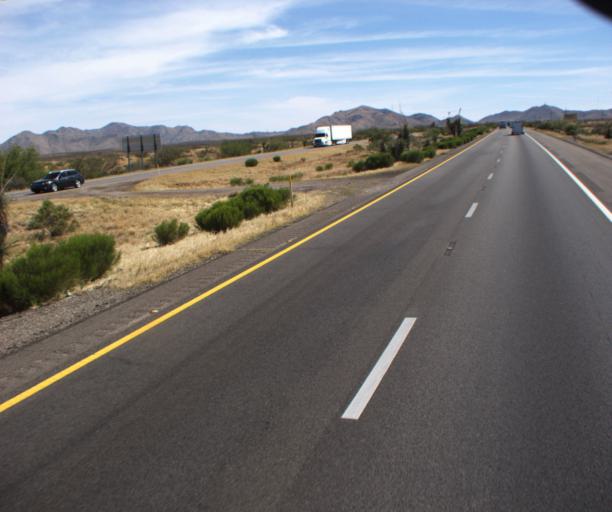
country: US
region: Arizona
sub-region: Cochise County
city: Saint David
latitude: 31.9868
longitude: -110.1916
